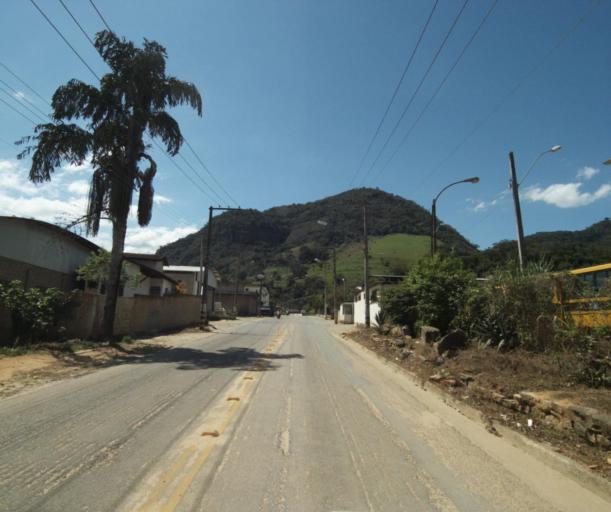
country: BR
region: Espirito Santo
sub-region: Mimoso Do Sul
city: Mimoso do Sul
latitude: -21.0764
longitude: -41.3550
